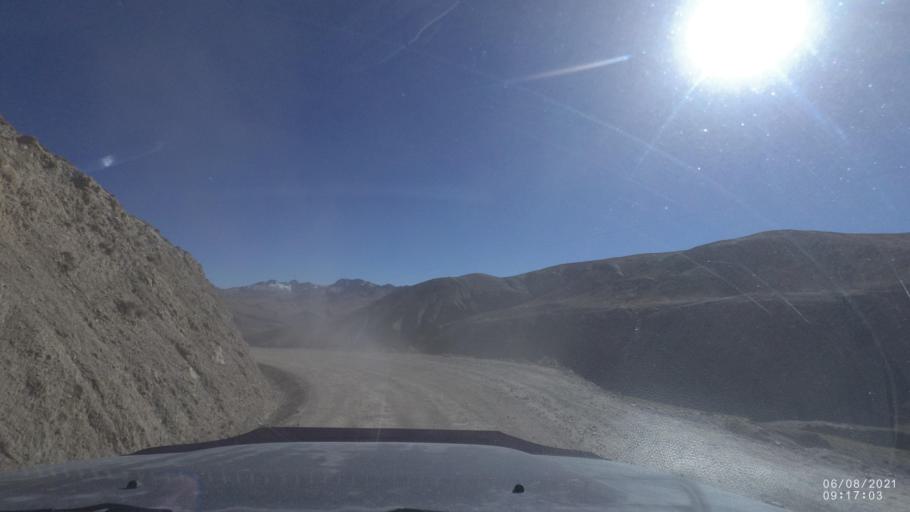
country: BO
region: Cochabamba
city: Colchani
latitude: -17.0433
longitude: -66.5265
